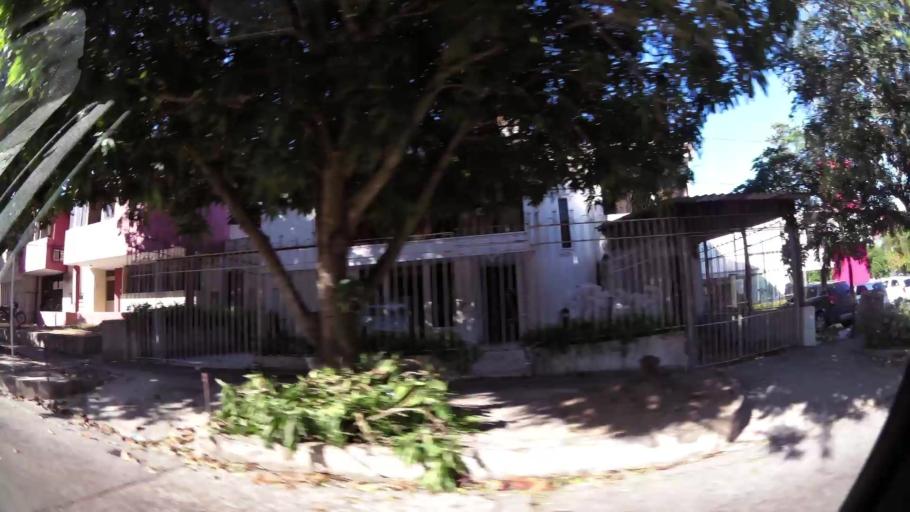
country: CO
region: Atlantico
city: Barranquilla
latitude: 11.0039
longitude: -74.8275
